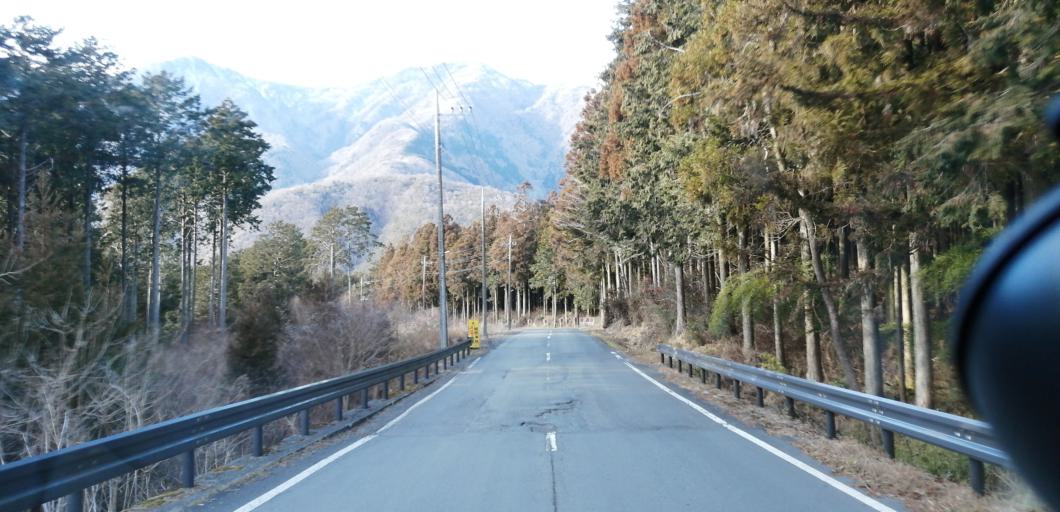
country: JP
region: Yamanashi
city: Fujikawaguchiko
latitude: 35.4041
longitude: 138.5869
